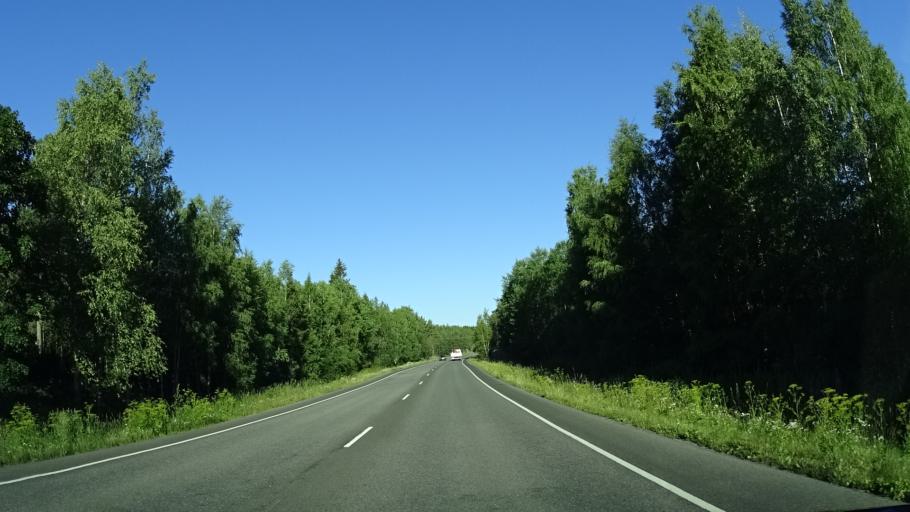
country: FI
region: Varsinais-Suomi
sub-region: Turku
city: Naantali
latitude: 60.4596
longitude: 21.9548
